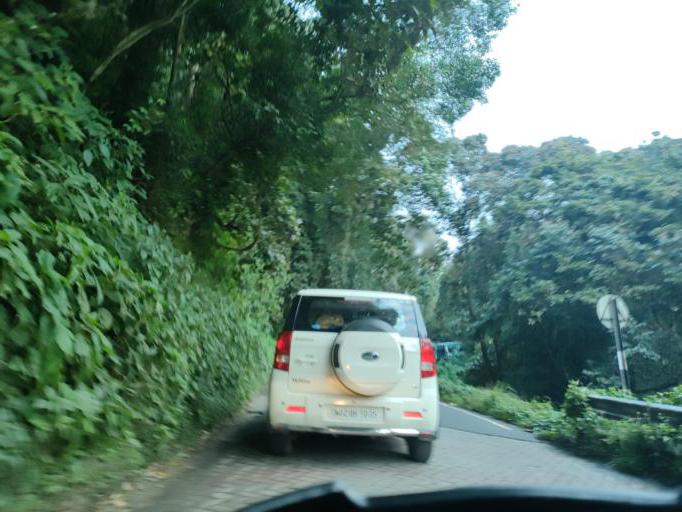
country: IN
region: Tamil Nadu
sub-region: Dindigul
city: Kodaikanal
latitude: 10.2510
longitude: 77.5220
